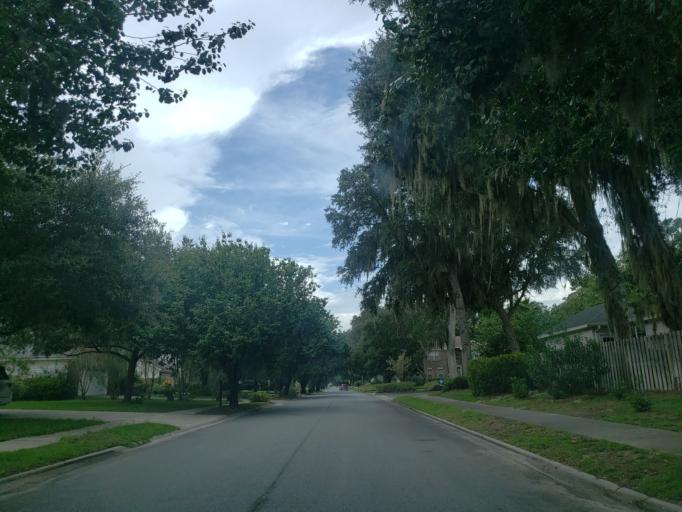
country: US
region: Georgia
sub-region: Chatham County
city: Wilmington Island
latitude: 31.9974
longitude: -80.9758
